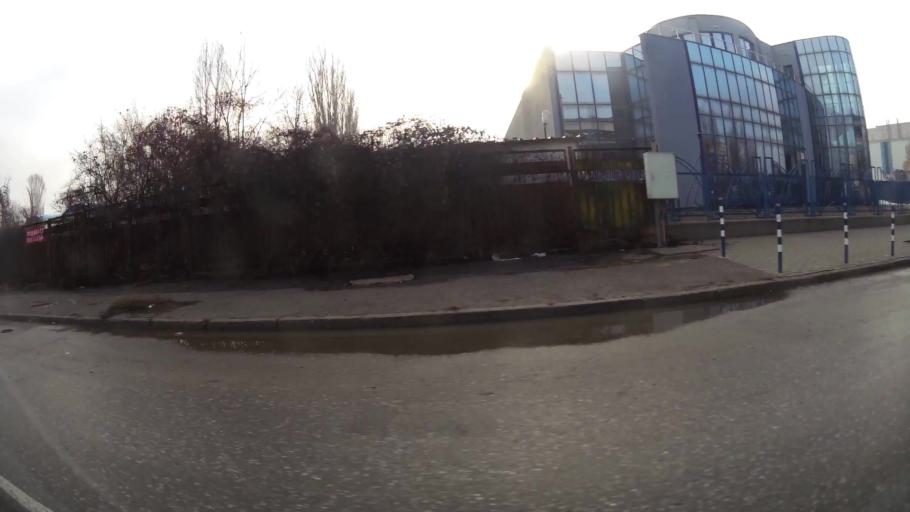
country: BG
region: Sofia-Capital
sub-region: Stolichna Obshtina
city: Sofia
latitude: 42.7374
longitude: 23.3258
